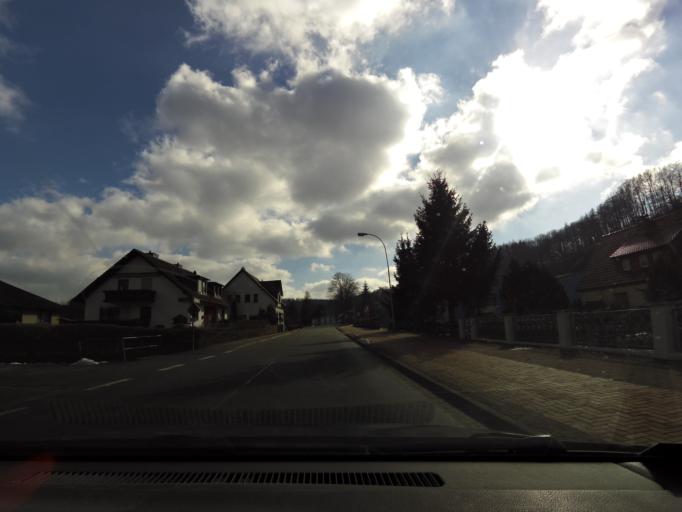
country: DE
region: Lower Saxony
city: Bad Lauterberg im Harz
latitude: 51.6227
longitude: 10.4336
